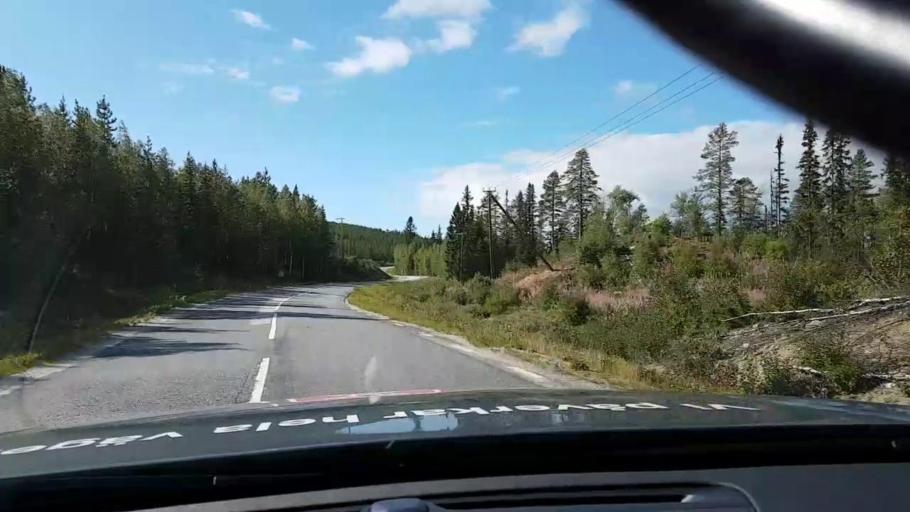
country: SE
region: Vaesterbotten
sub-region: Asele Kommun
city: Asele
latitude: 63.8281
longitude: 17.4701
